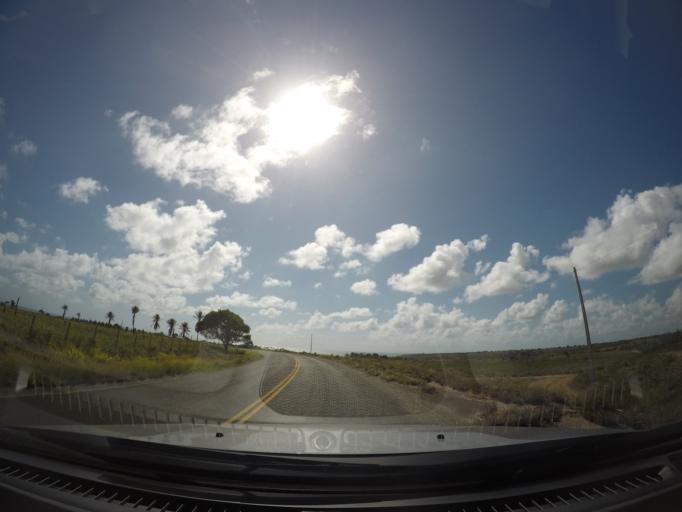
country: BR
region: Paraiba
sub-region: Pitimbu
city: Pitimbu
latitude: -7.3918
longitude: -34.8219
